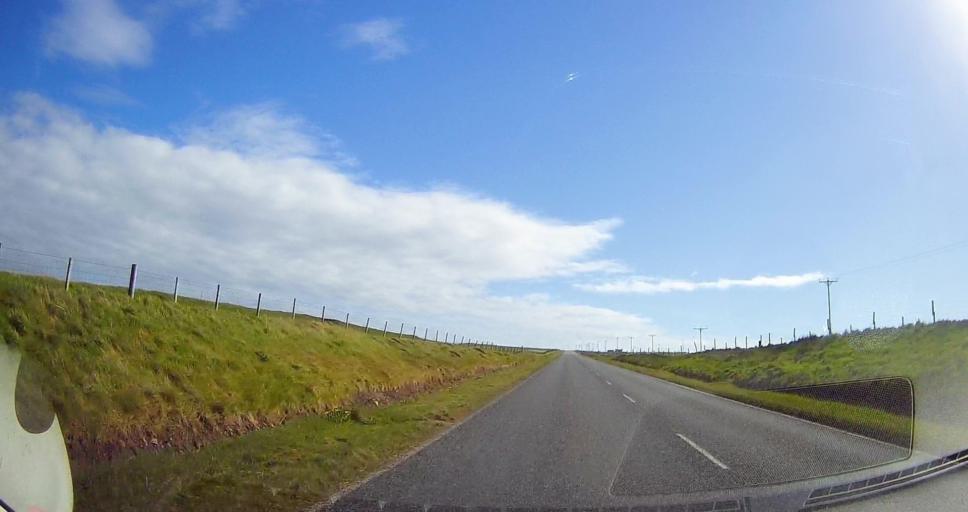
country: GB
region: Scotland
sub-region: Shetland Islands
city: Sandwick
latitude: 59.9046
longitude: -1.3025
